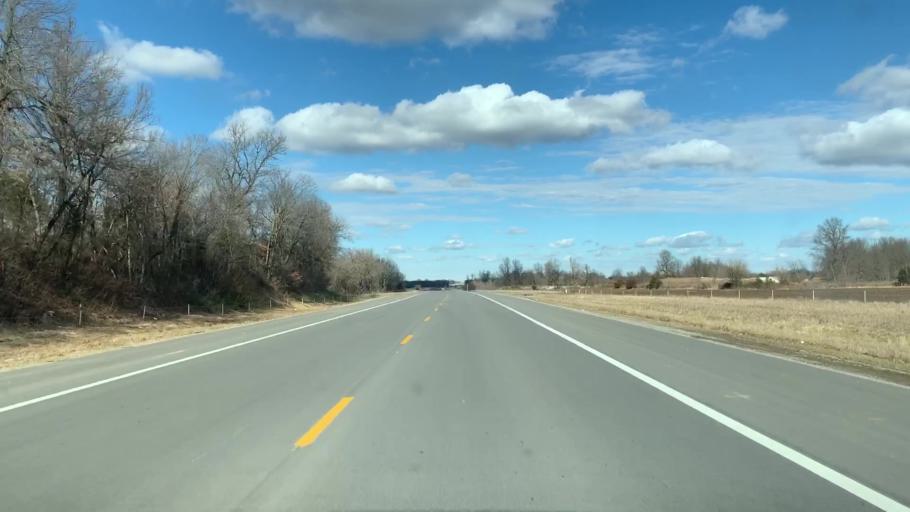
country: US
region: Kansas
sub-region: Cherokee County
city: Columbus
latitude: 37.2579
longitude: -94.8319
